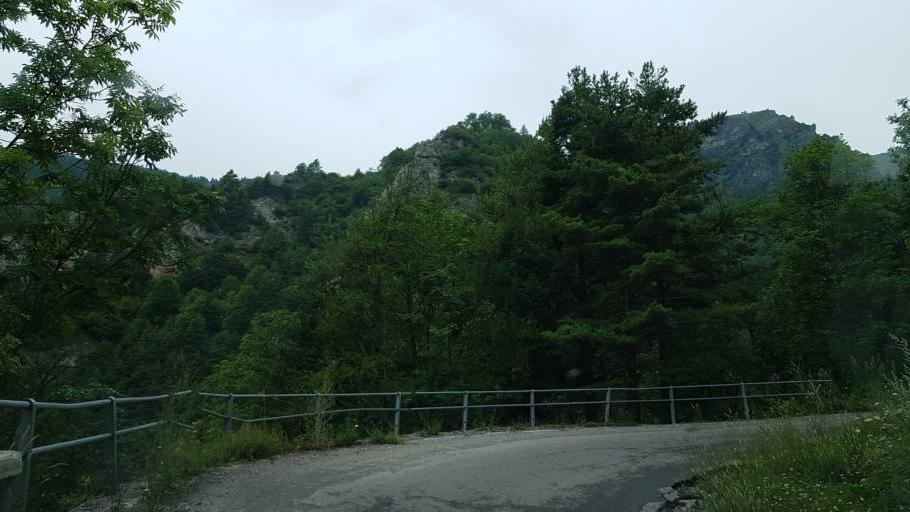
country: IT
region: Piedmont
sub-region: Provincia di Cuneo
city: Stroppo
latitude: 44.5134
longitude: 7.1260
